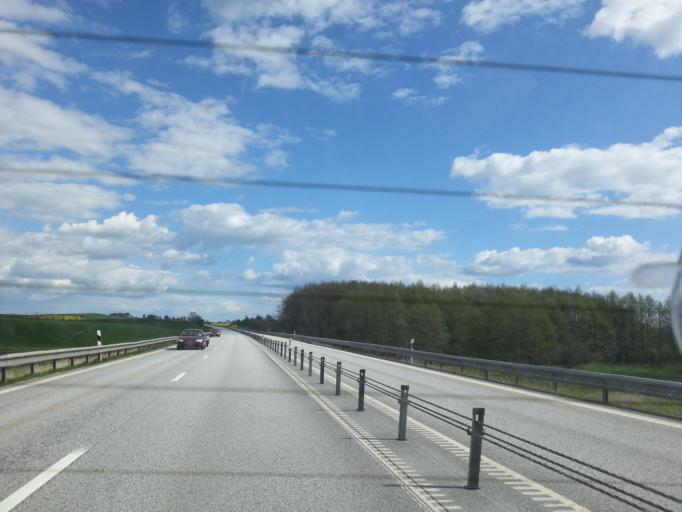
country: SE
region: Skane
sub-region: Ystads Kommun
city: Ystad
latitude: 55.4599
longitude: 13.7298
